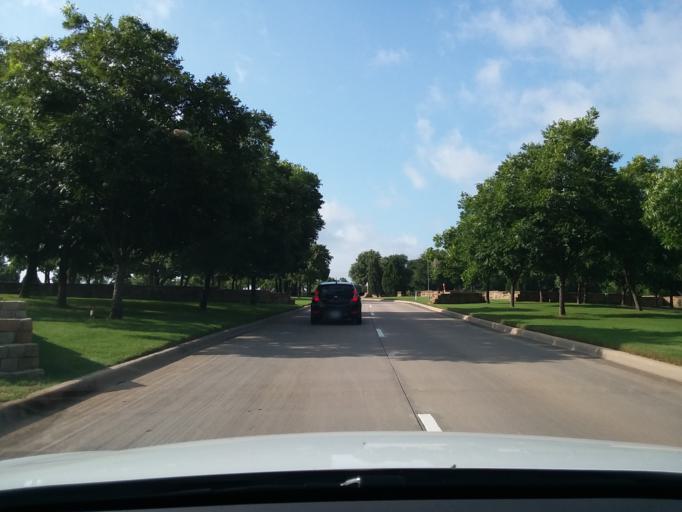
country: US
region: Texas
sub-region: Denton County
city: Bartonville
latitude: 33.0758
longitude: -97.1235
